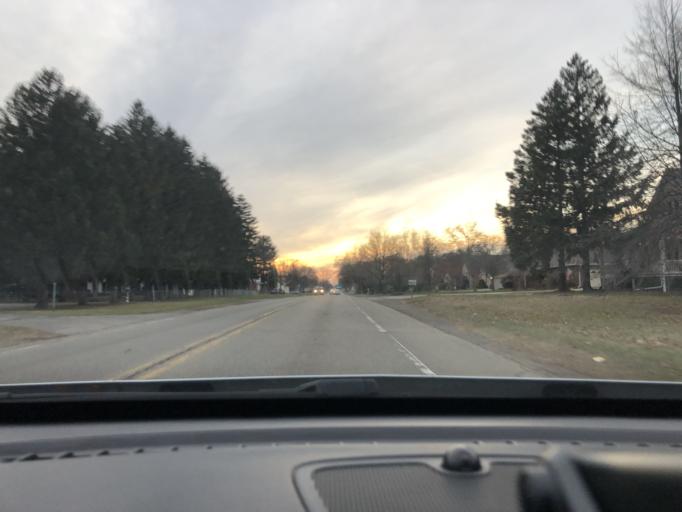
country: US
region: Michigan
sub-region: Wayne County
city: Taylor
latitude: 42.2413
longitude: -83.2602
